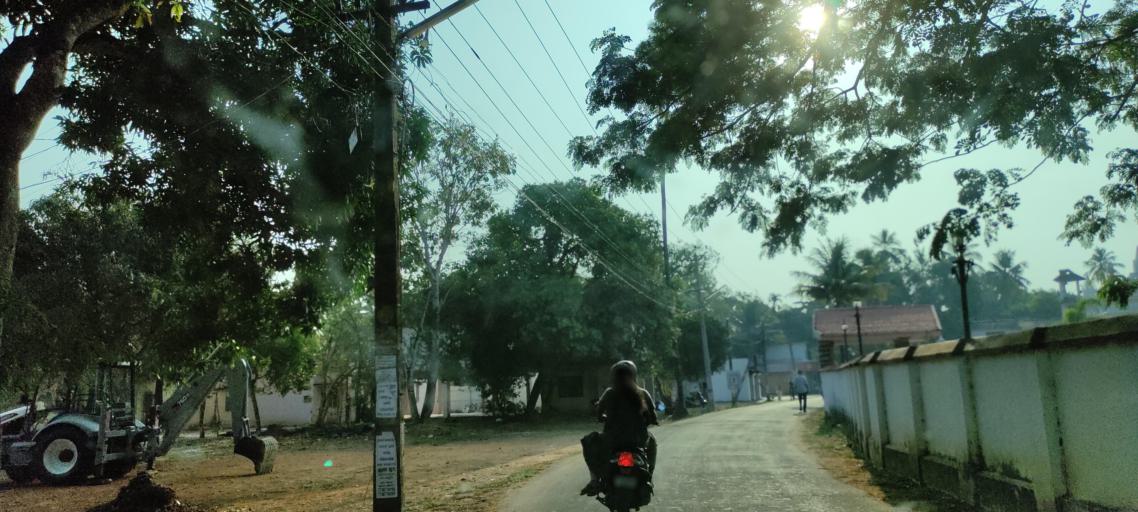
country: IN
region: Kerala
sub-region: Alappuzha
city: Alleppey
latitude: 9.5286
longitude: 76.3203
